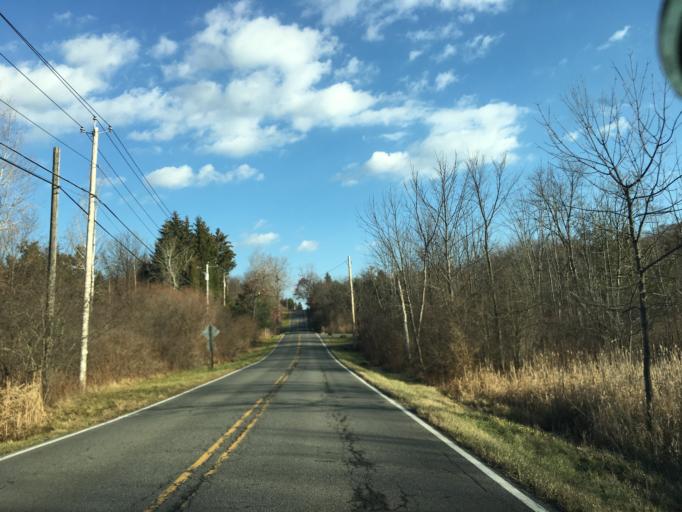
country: US
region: New York
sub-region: Rensselaer County
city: East Greenbush
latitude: 42.6315
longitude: -73.6843
